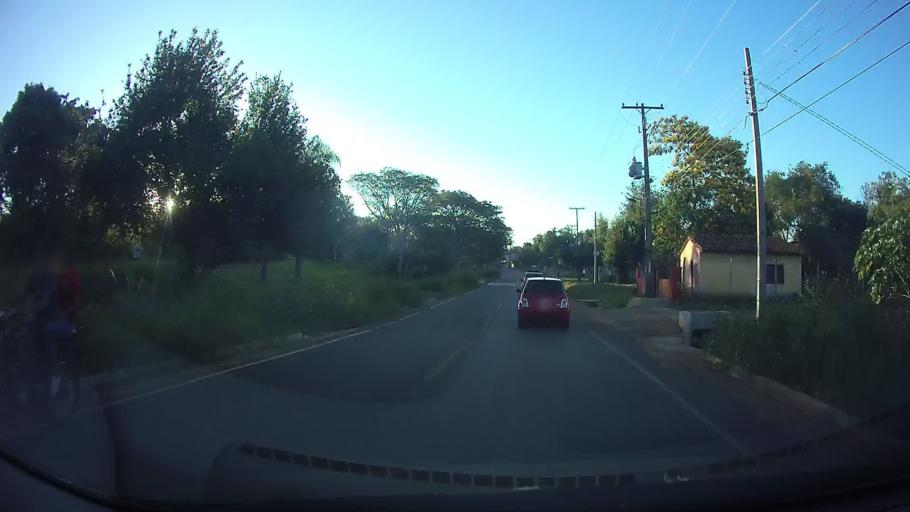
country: PY
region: Central
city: Limpio
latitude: -25.2545
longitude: -57.4591
